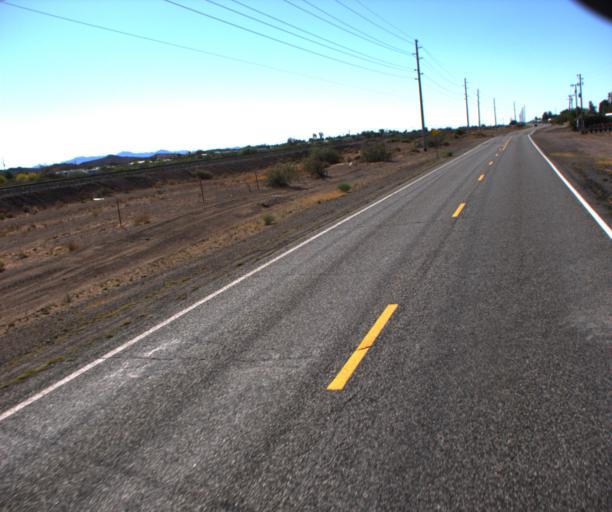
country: US
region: Arizona
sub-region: La Paz County
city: Cienega Springs
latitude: 33.9400
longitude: -114.0114
